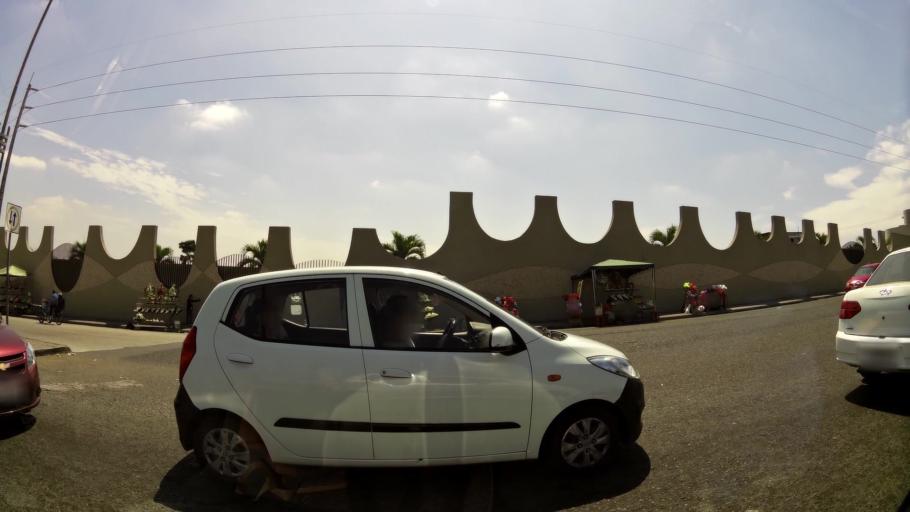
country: EC
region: Guayas
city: Guayaquil
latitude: -2.1342
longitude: -79.9220
